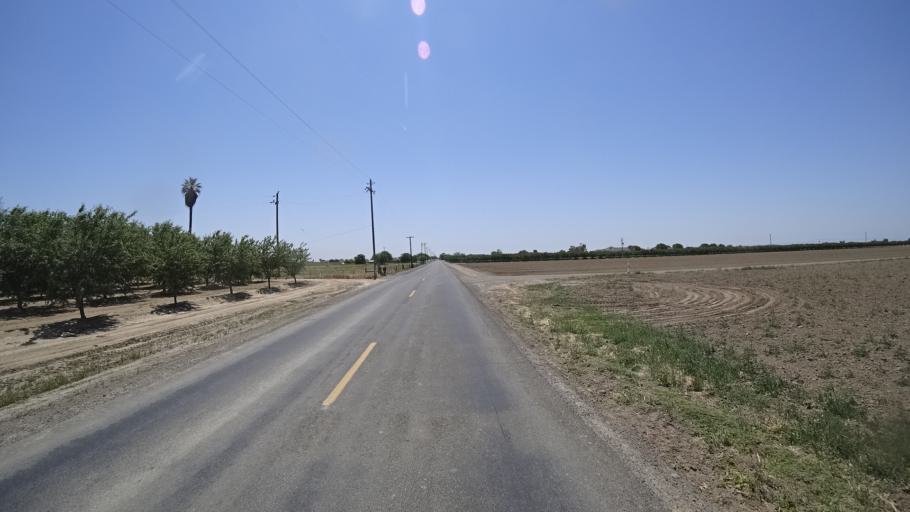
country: US
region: California
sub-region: Kings County
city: Lemoore
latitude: 36.2624
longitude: -119.7630
